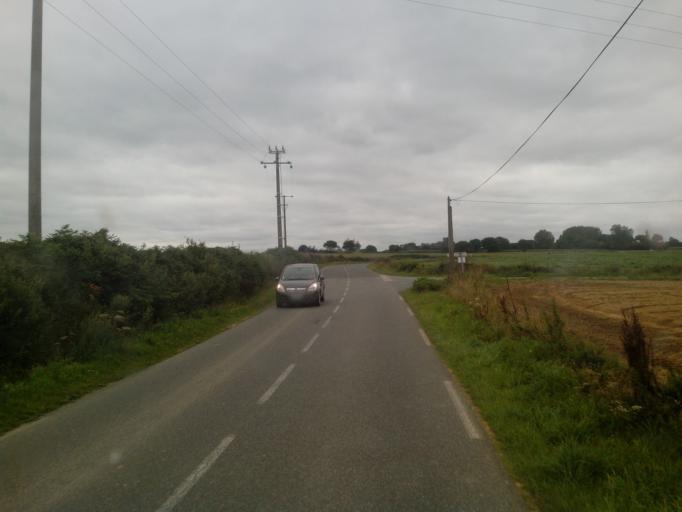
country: FR
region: Brittany
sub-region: Departement des Cotes-d'Armor
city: Plouezec
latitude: 48.7198
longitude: -2.9795
